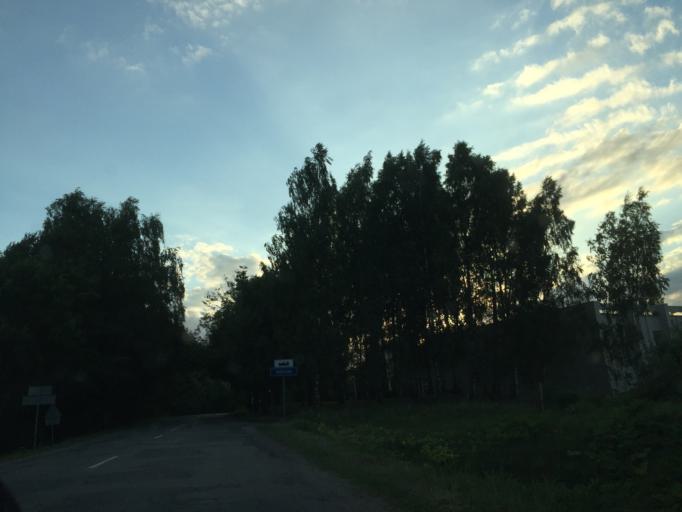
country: LV
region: Sigulda
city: Sigulda
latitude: 57.1401
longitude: 24.8695
